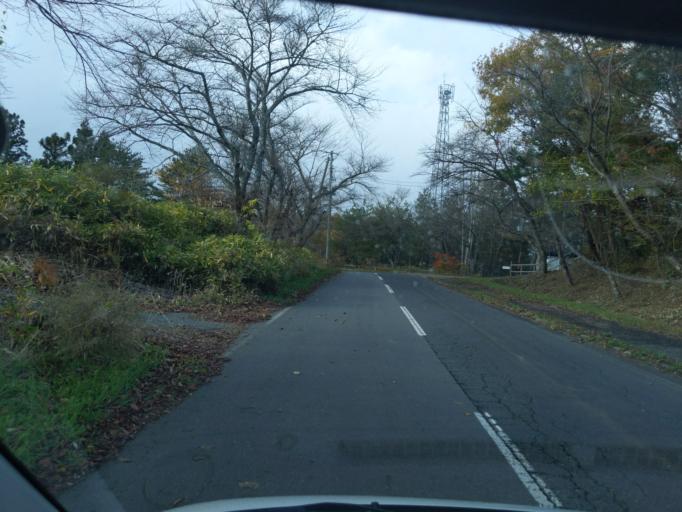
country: JP
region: Iwate
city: Mizusawa
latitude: 39.0375
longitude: 141.0835
